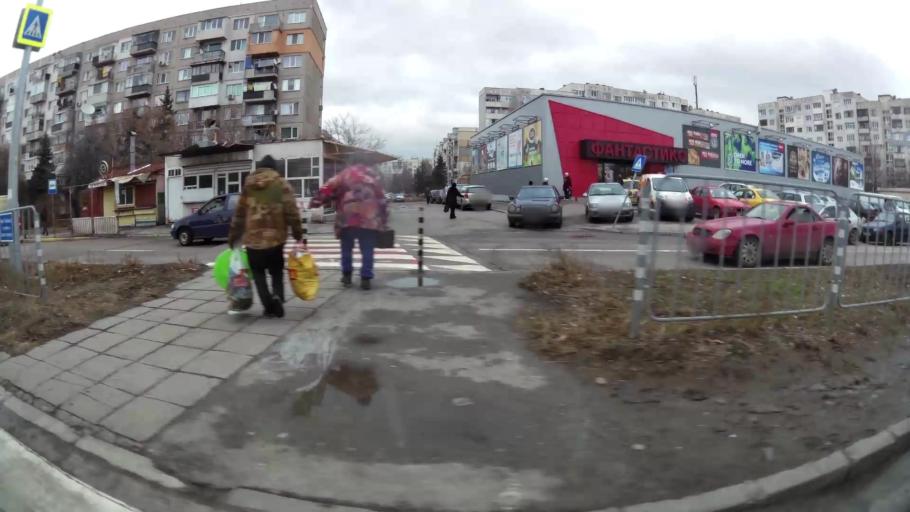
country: BG
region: Sofia-Capital
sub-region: Stolichna Obshtina
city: Sofia
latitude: 42.7306
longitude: 23.2867
